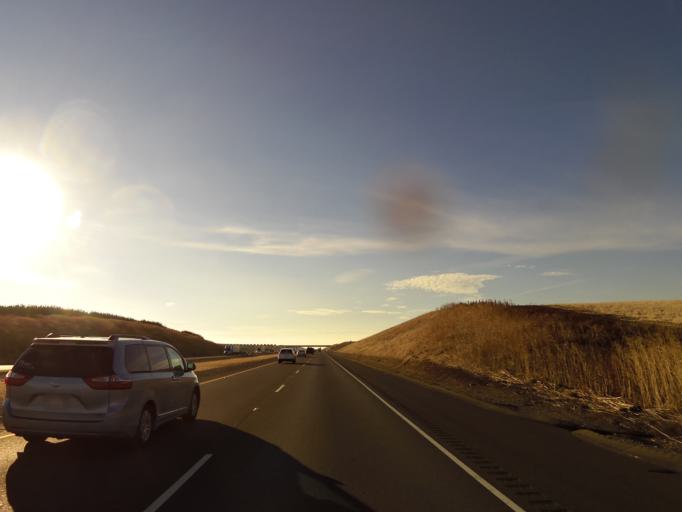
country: US
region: California
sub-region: Stanislaus County
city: Newman
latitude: 37.3596
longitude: -121.1213
